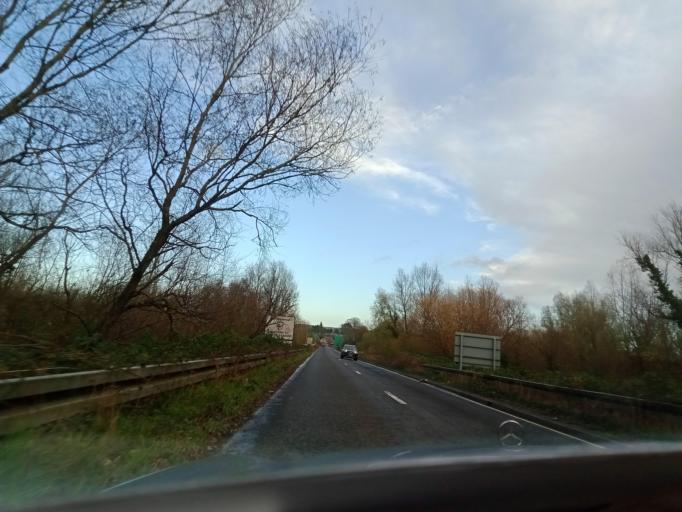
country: IE
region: Leinster
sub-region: Kilkenny
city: Piltown
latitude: 52.3260
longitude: -7.3189
